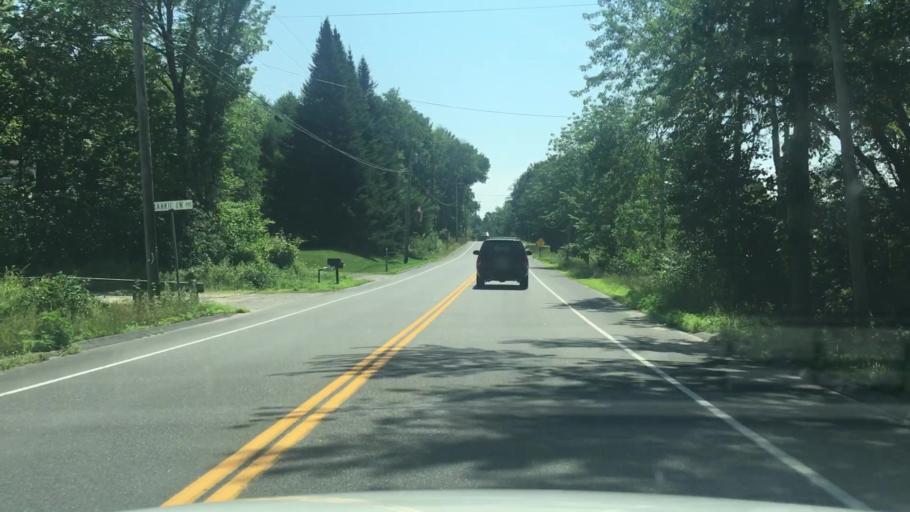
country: US
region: Maine
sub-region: Cumberland County
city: Cumberland Center
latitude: 43.8039
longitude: -70.2732
